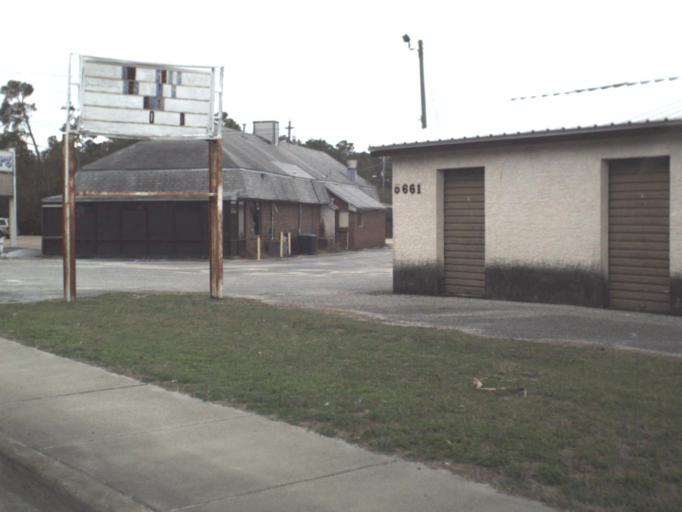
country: US
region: Florida
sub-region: Bay County
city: Parker
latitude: 30.1216
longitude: -85.5925
